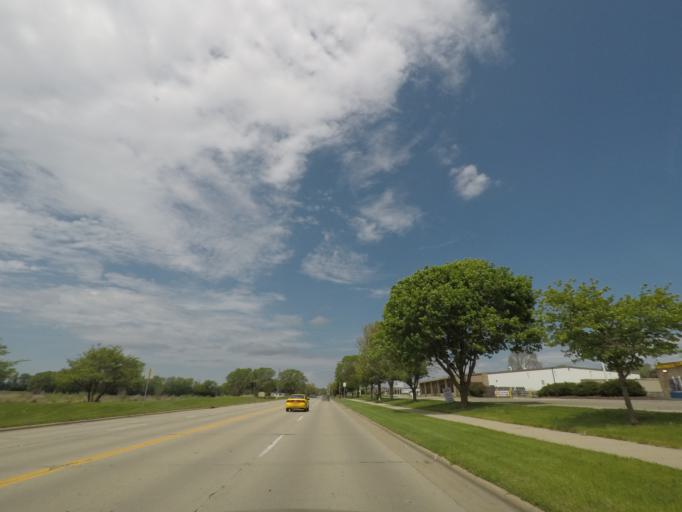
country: US
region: Wisconsin
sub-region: Rock County
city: Beloit
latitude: 42.5194
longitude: -89.0668
